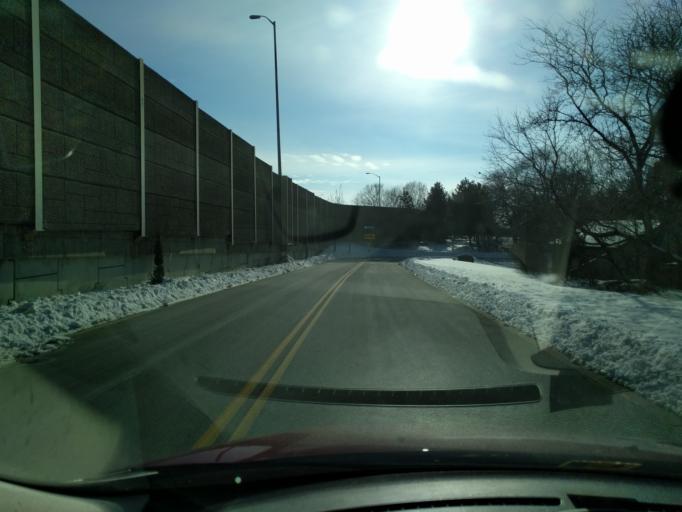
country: US
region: Wisconsin
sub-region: Milwaukee County
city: Whitefish Bay
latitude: 43.1265
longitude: -87.9139
